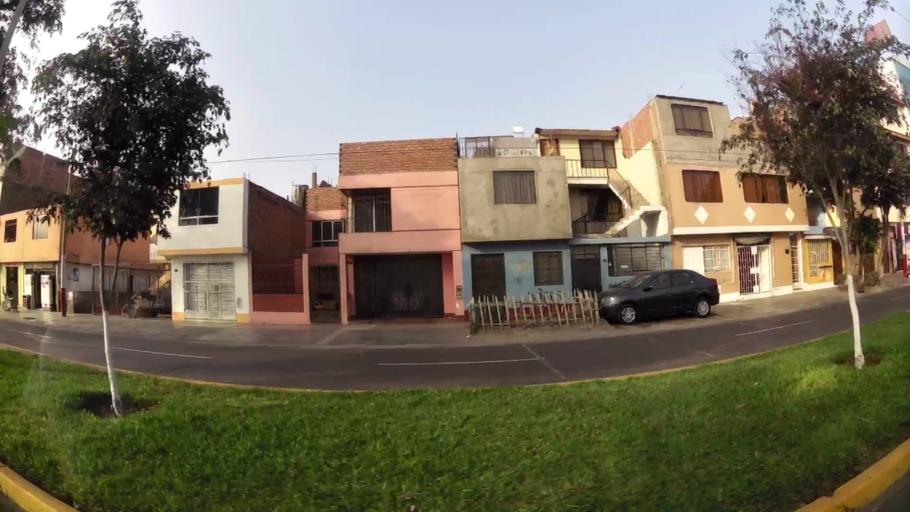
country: PE
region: Callao
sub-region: Callao
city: Callao
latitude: -12.0085
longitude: -77.0979
